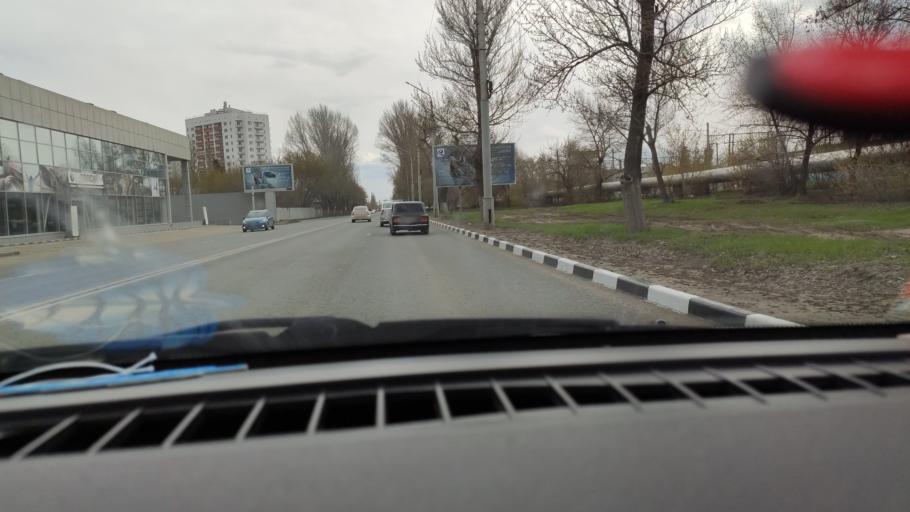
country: RU
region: Saratov
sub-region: Saratovskiy Rayon
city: Saratov
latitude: 51.5721
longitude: 45.9928
